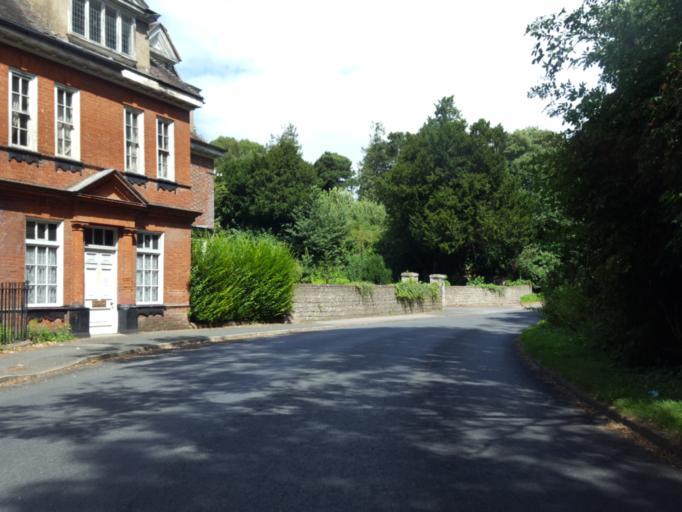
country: GB
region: England
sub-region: Kent
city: West Malling
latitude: 51.2881
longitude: 0.4029
